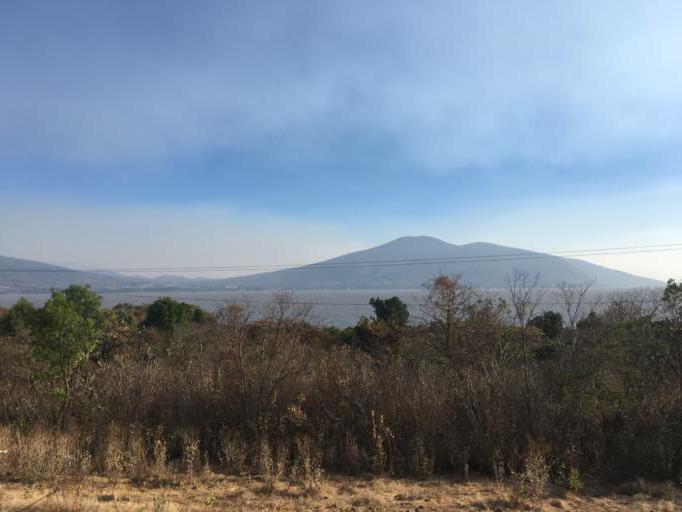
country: MX
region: Michoacan
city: Santa Fe de la Laguna
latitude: 19.6710
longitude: -101.5717
